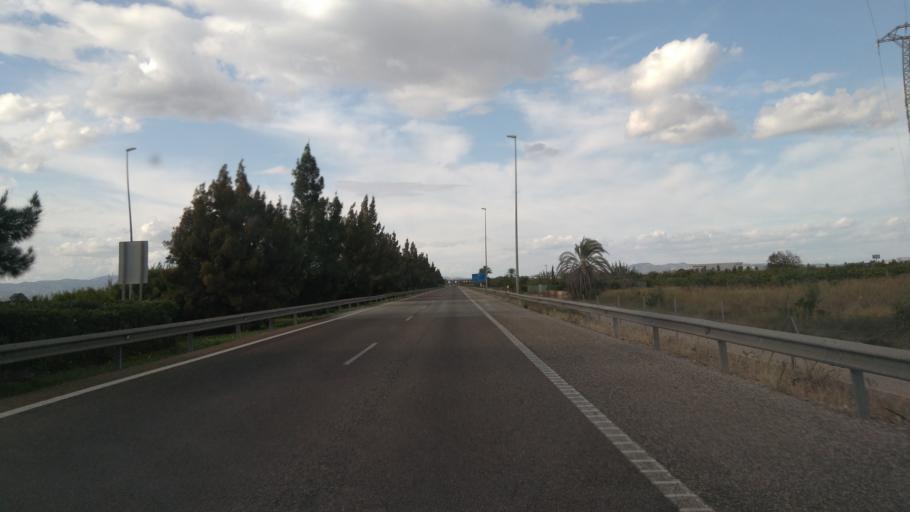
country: ES
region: Valencia
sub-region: Provincia de Valencia
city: Guadassuar
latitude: 39.1646
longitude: -0.4582
